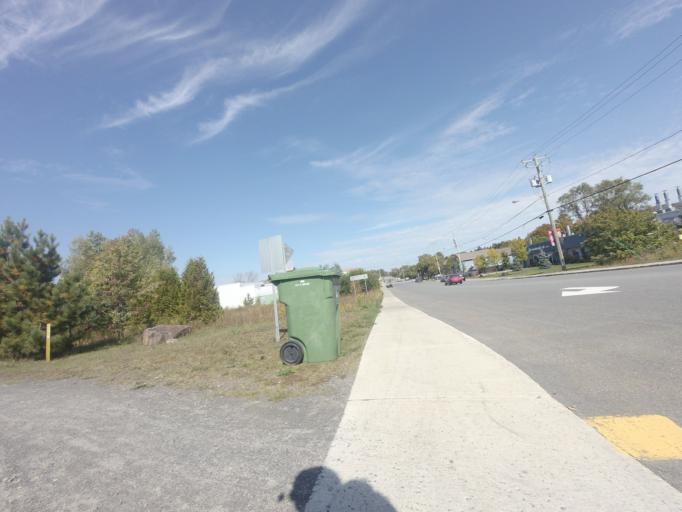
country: CA
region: Quebec
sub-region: Laurentides
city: Sainte-Agathe-des-Monts
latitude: 46.0498
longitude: -74.2801
